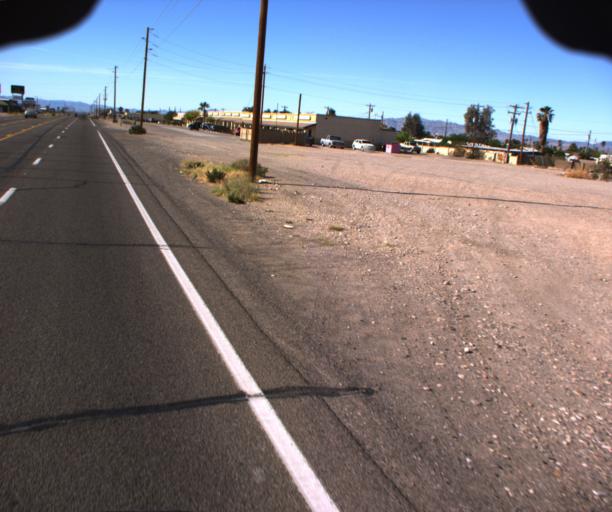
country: US
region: Arizona
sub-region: Mohave County
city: Mohave Valley
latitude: 34.9965
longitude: -114.5981
